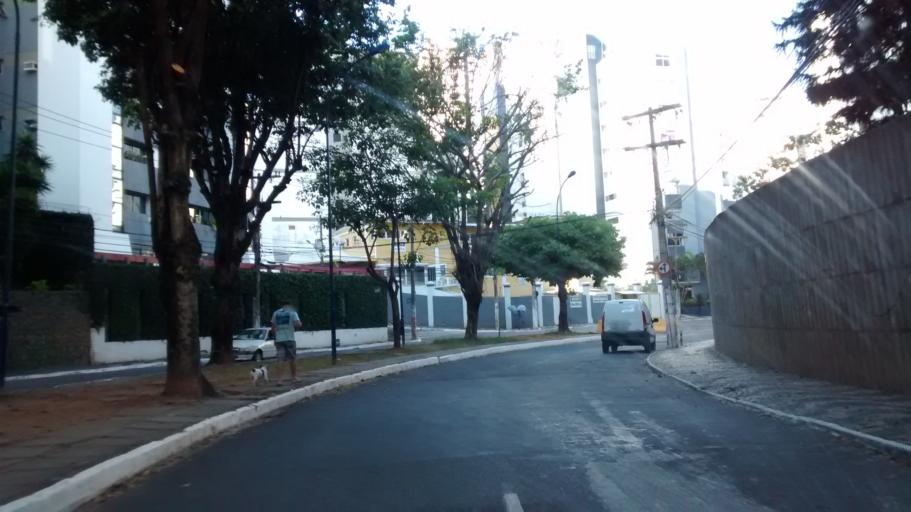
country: BR
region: Bahia
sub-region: Salvador
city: Salvador
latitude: -13.0043
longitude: -38.5193
